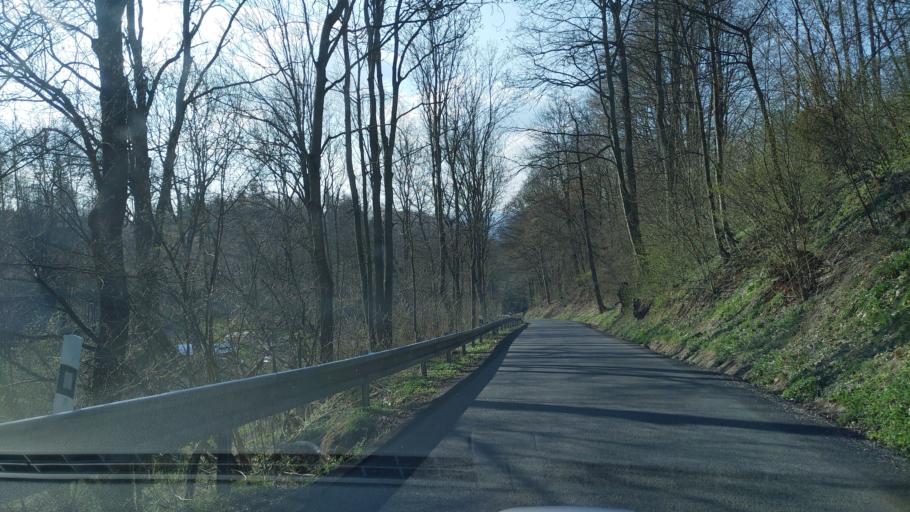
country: CZ
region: Ustecky
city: Vernerice
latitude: 50.6959
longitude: 14.2470
